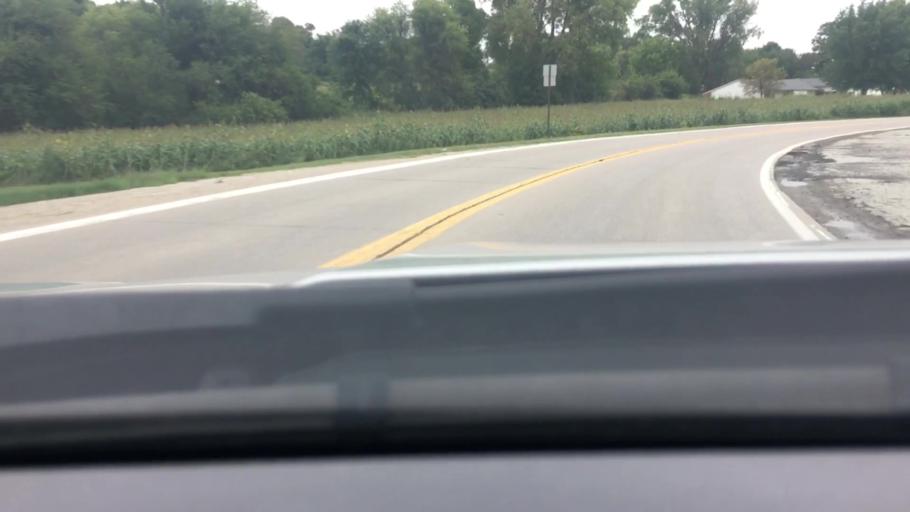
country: US
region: Iowa
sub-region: Pottawattamie County
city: Council Bluffs
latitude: 41.2602
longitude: -95.8053
